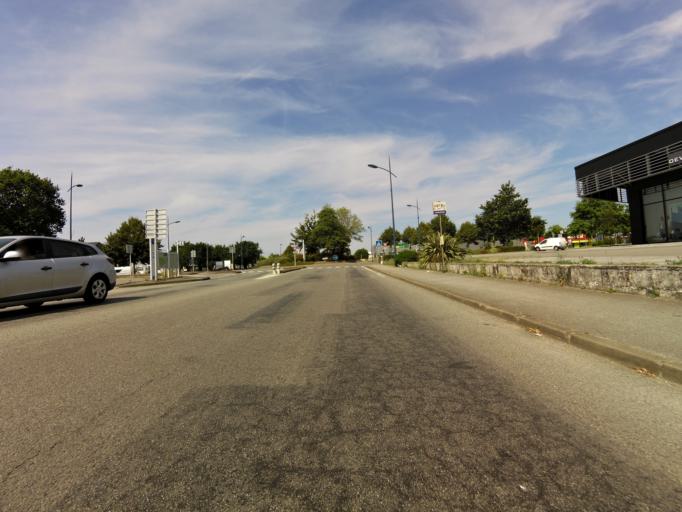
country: FR
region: Brittany
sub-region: Departement du Morbihan
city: Auray
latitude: 47.6633
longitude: -3.0062
